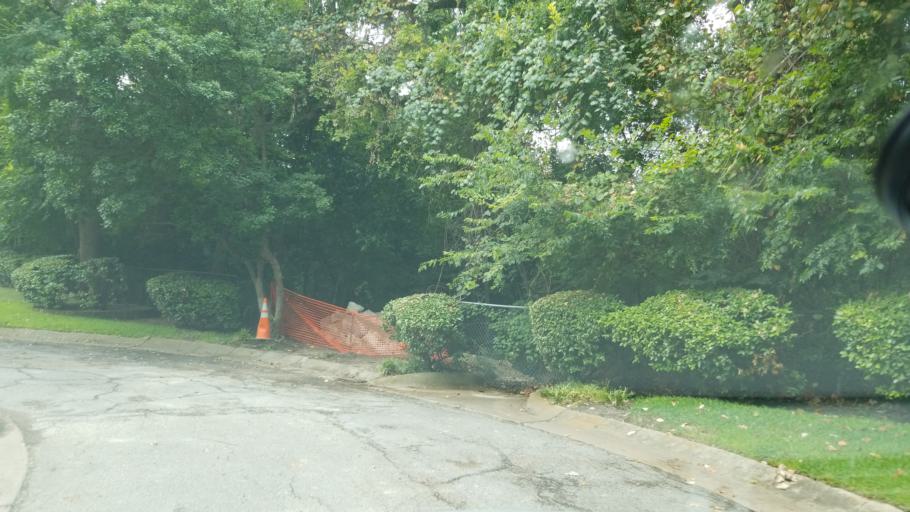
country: US
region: Texas
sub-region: Dallas County
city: Duncanville
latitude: 32.6693
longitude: -96.8552
